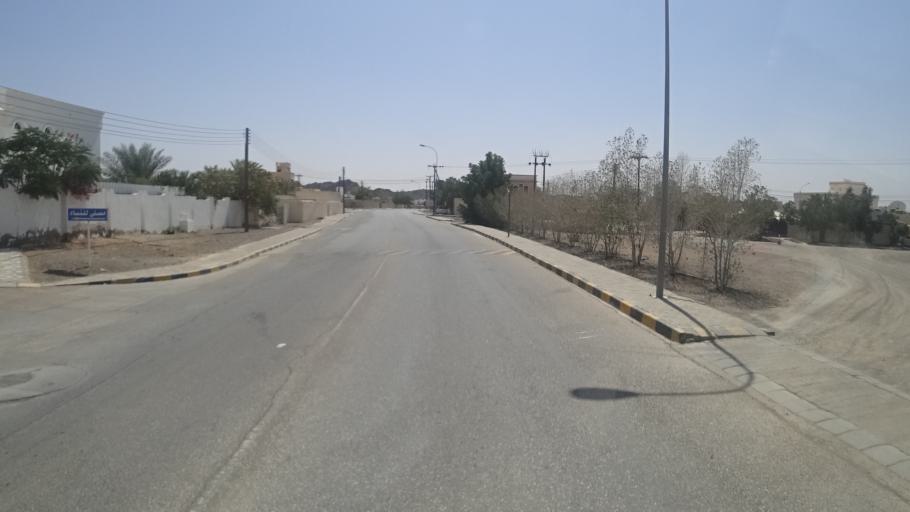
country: OM
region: Ash Sharqiyah
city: Ibra'
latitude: 22.6844
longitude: 58.5439
